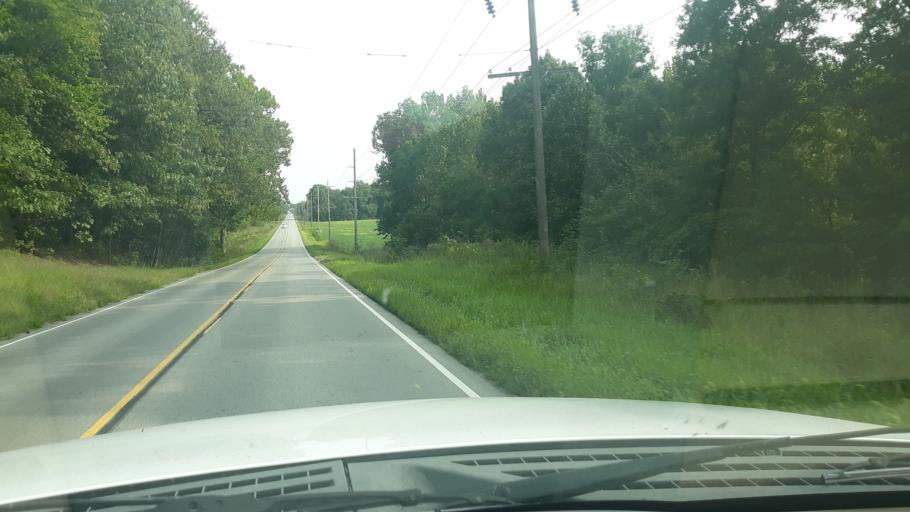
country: US
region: Illinois
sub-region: White County
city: Norris City
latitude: 37.9298
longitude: -88.3479
